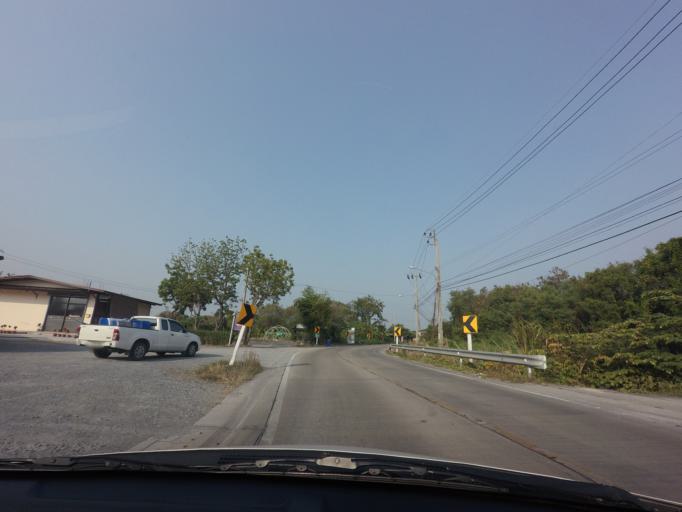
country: TH
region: Nonthaburi
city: Bang Yai
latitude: 13.8050
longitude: 100.3902
